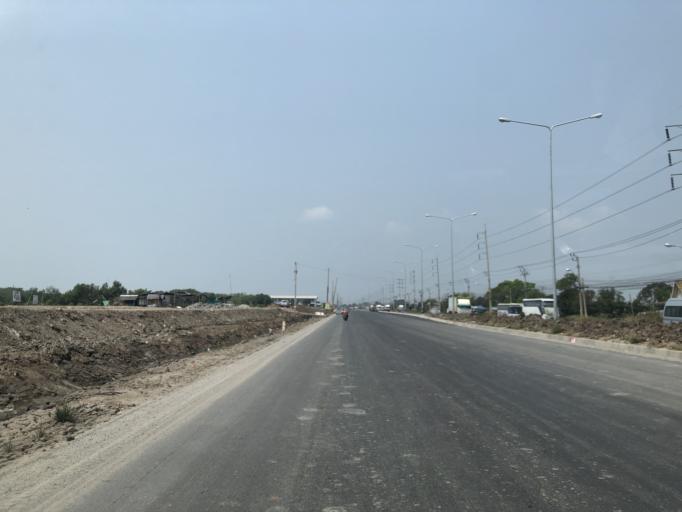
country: TH
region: Samut Prakan
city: Bang Bo
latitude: 13.5108
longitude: 100.7991
